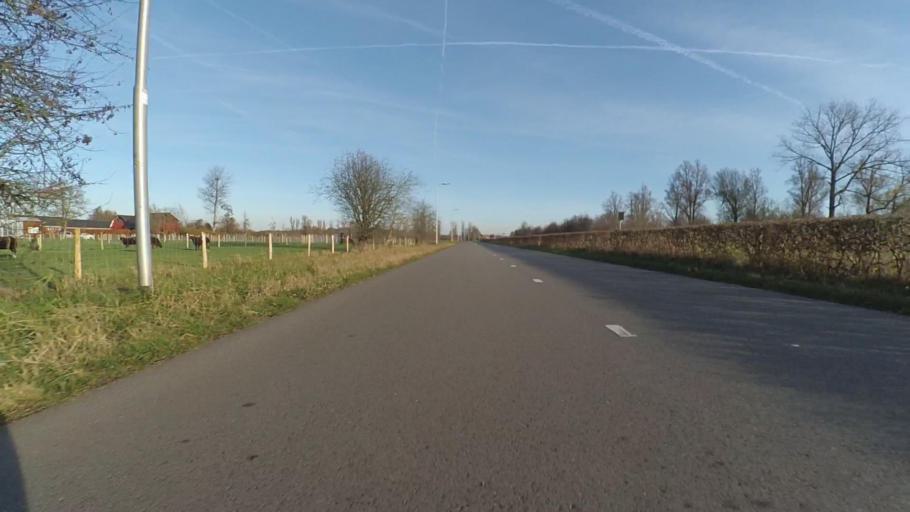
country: NL
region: Utrecht
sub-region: Gemeente Wijk bij Duurstede
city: Wijk bij Duurstede
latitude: 52.0032
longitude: 5.3165
